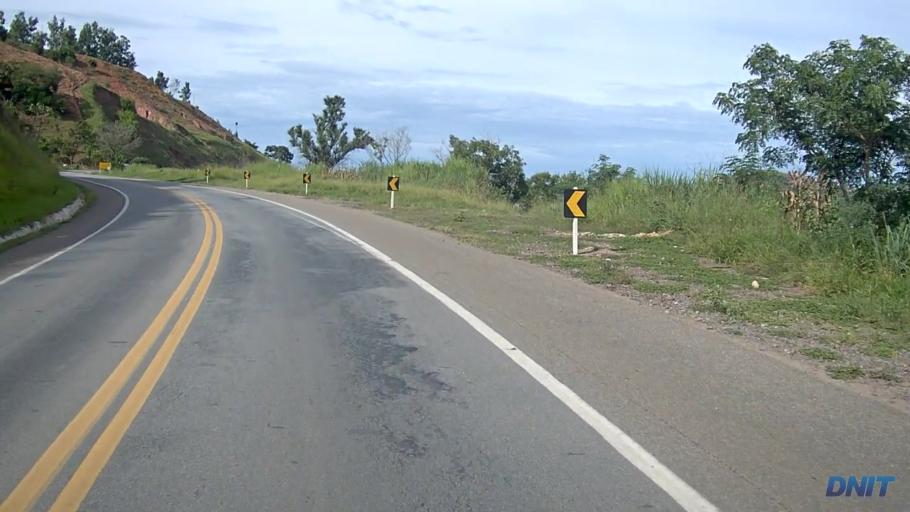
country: BR
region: Minas Gerais
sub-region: Belo Oriente
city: Belo Oriente
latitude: -19.1639
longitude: -42.2420
